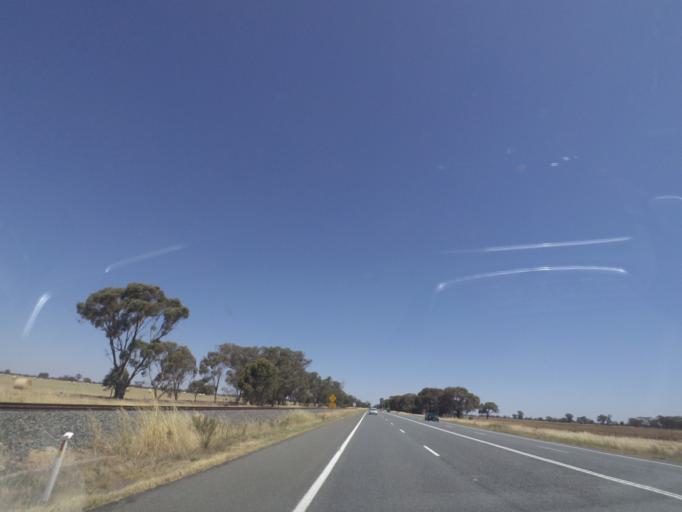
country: AU
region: Victoria
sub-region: Greater Shepparton
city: Shepparton
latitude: -36.1929
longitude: 145.4319
